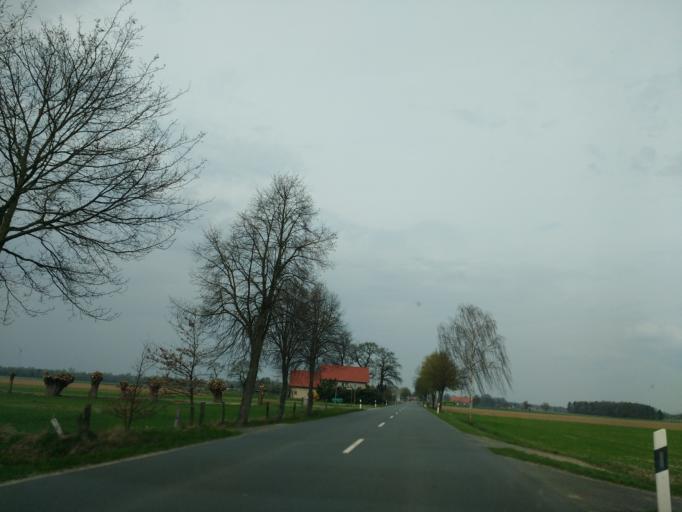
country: DE
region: North Rhine-Westphalia
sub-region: Regierungsbezirk Detmold
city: Salzkotten
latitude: 51.7280
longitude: 8.6632
